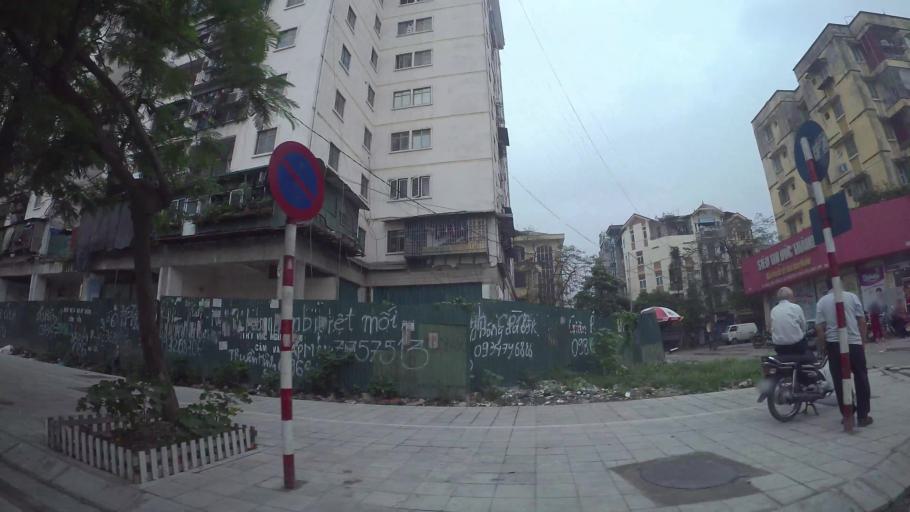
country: VN
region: Ha Noi
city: Hai BaTrung
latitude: 20.9837
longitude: 105.8593
